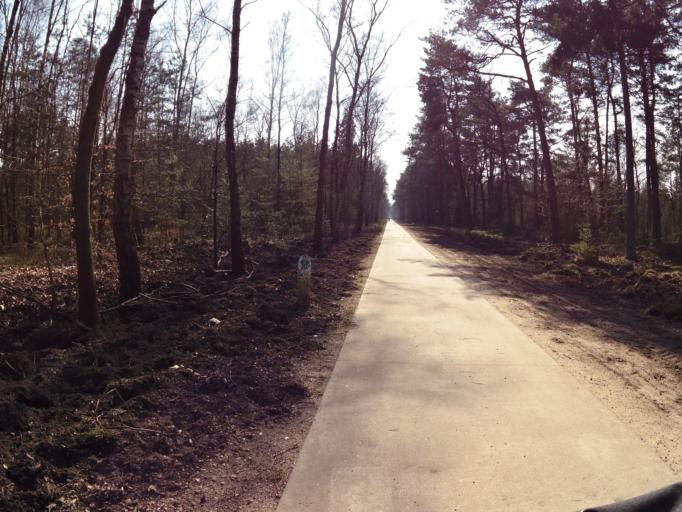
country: NL
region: Gelderland
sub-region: Gemeente Epe
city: Epe
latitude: 52.3724
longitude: 5.9596
